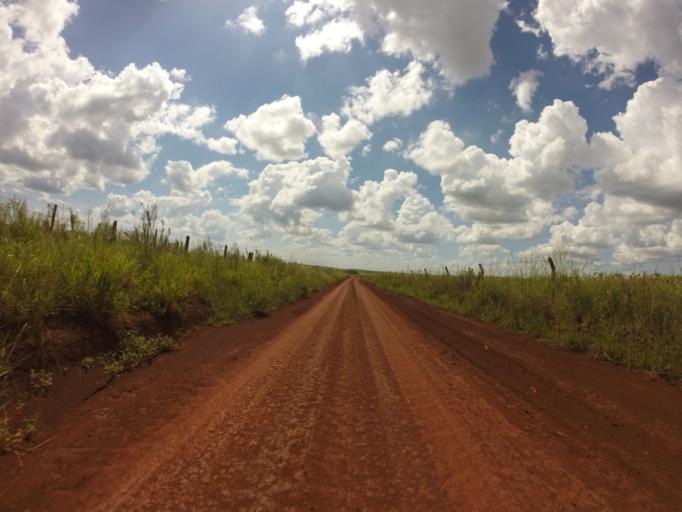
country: PY
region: Alto Parana
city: Ciudad del Este
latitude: -25.3367
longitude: -54.6869
